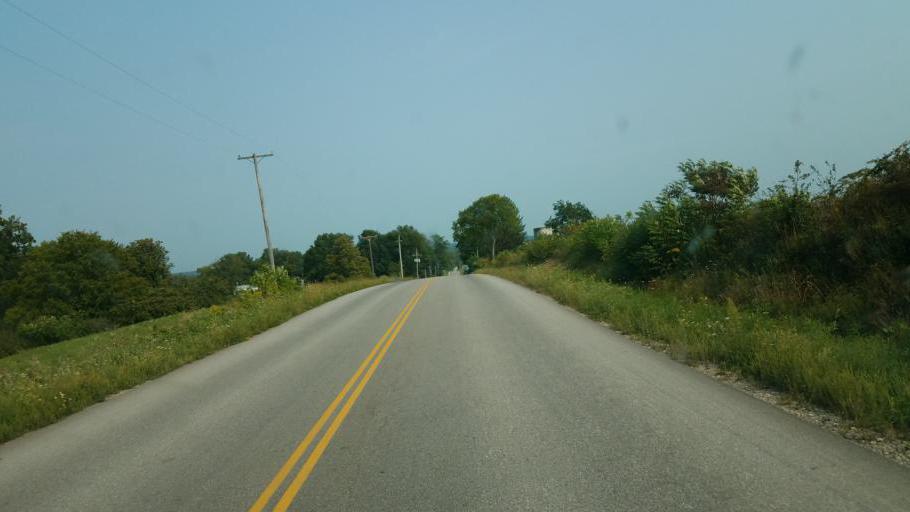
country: US
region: Ohio
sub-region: Ashtabula County
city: Orwell
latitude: 41.5085
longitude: -80.9497
